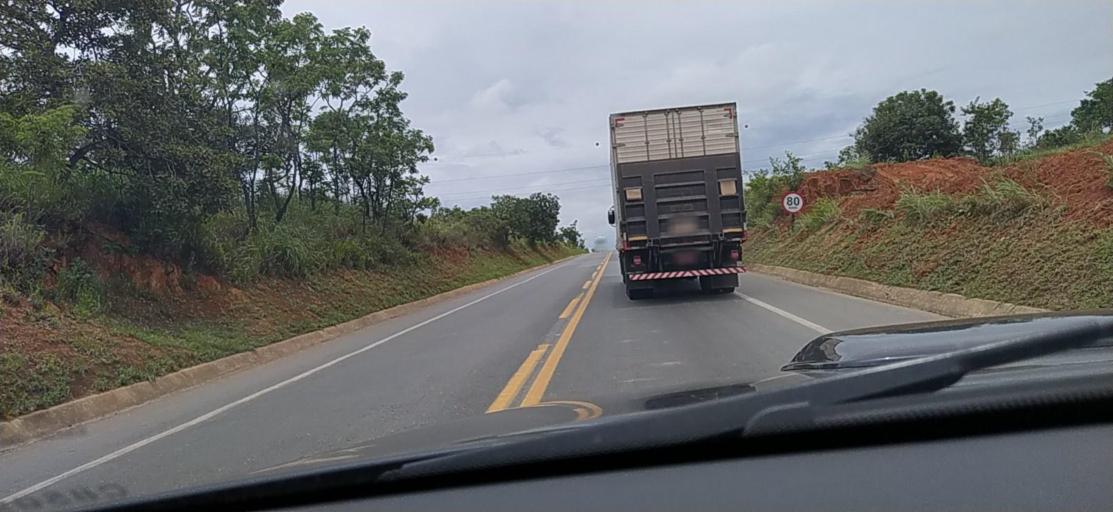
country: BR
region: Minas Gerais
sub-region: Curvelo
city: Curvelo
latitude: -18.7330
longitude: -44.4427
